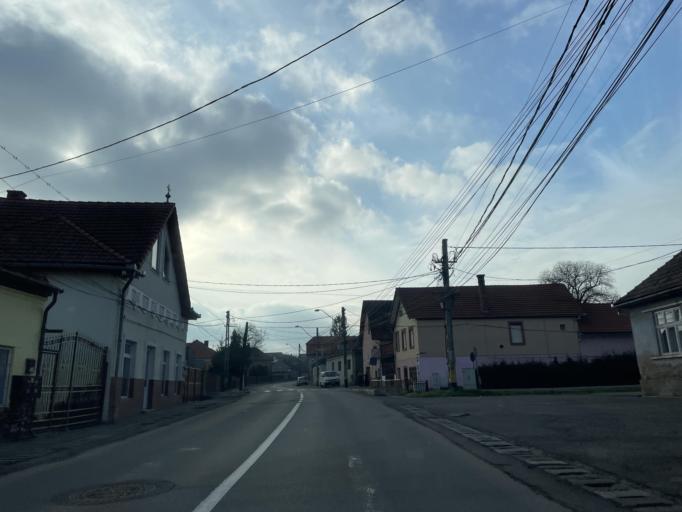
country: RO
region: Mures
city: Reghin-Sat
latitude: 46.7868
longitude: 24.7094
